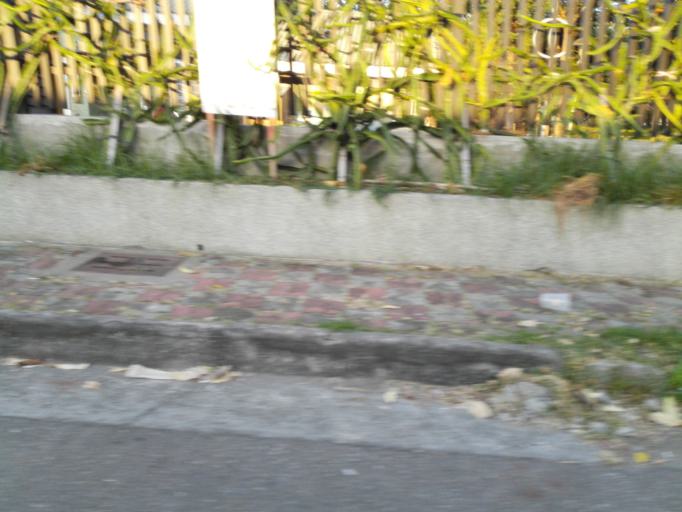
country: TW
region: Taiwan
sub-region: Taichung City
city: Taichung
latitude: 24.1736
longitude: 120.7225
